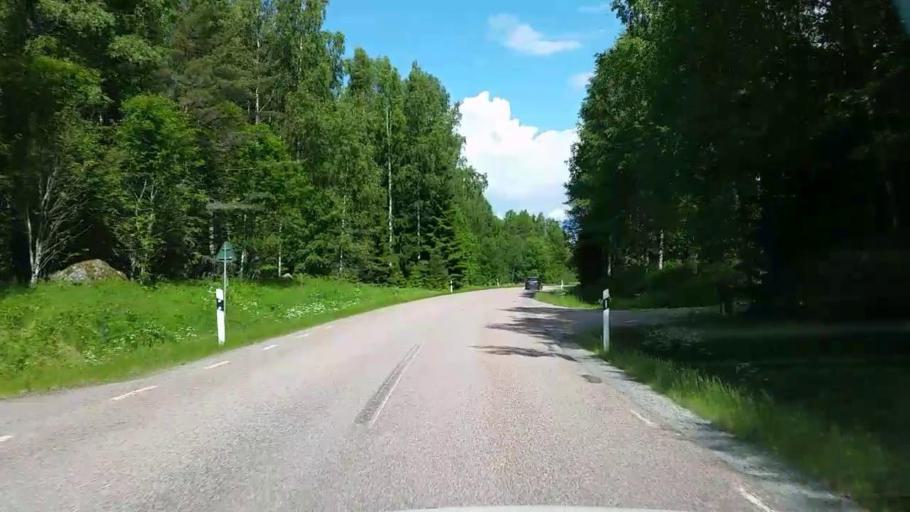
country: SE
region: Vaestmanland
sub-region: Fagersta Kommun
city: Fagersta
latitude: 59.9280
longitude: 15.8284
